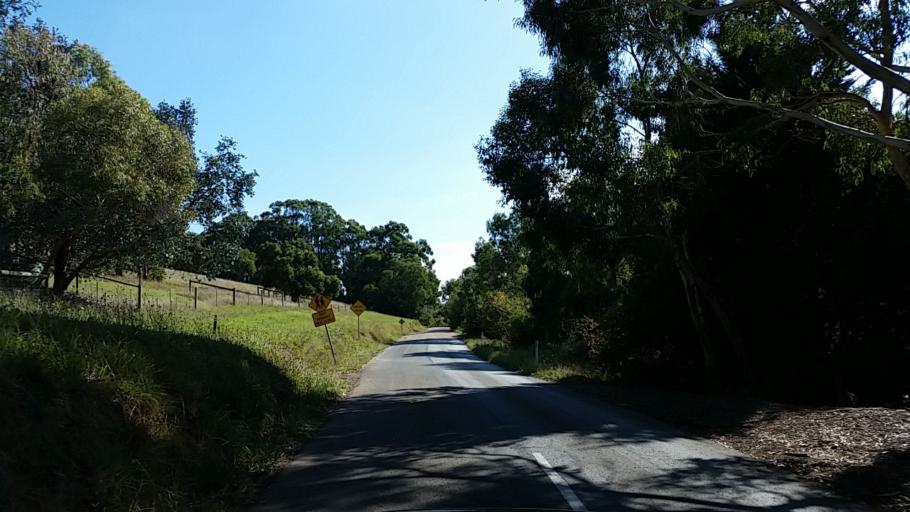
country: AU
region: South Australia
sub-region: Adelaide Hills
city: Adelaide Hills
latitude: -34.9556
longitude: 138.7180
